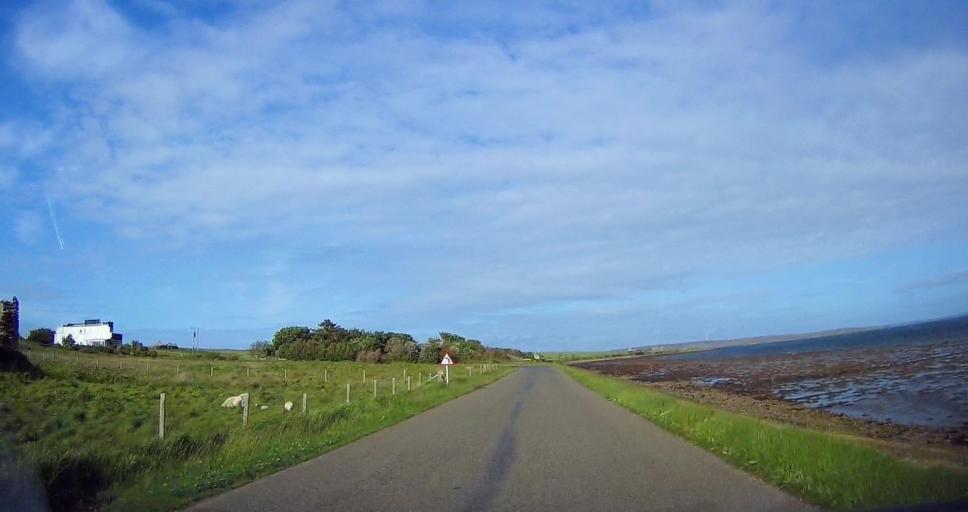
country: GB
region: Scotland
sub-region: Orkney Islands
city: Stromness
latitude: 58.8165
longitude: -3.2026
